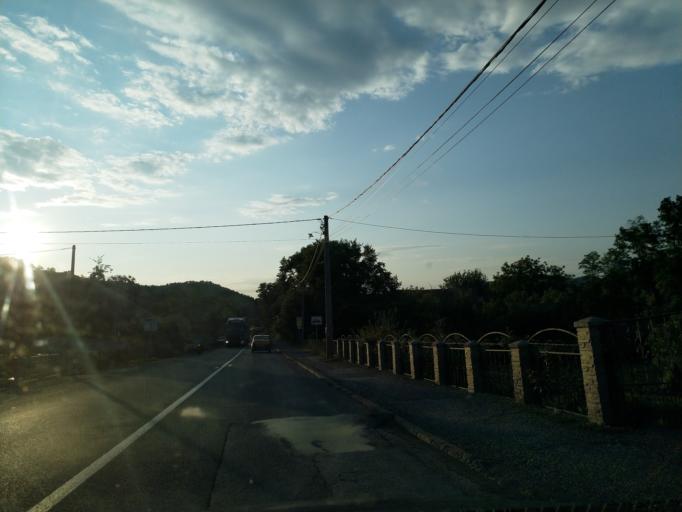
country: RS
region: Central Serbia
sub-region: Rasinski Okrug
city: Trstenik
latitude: 43.6167
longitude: 20.9826
